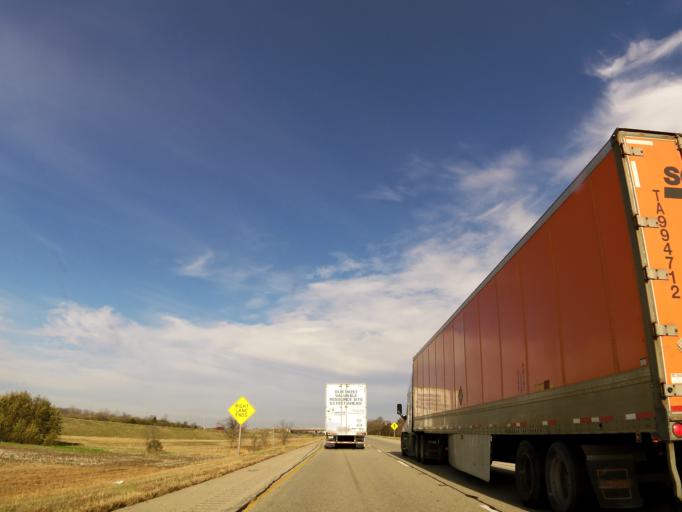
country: US
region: Illinois
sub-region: McLean County
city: Bloomington
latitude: 40.4435
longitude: -89.0190
